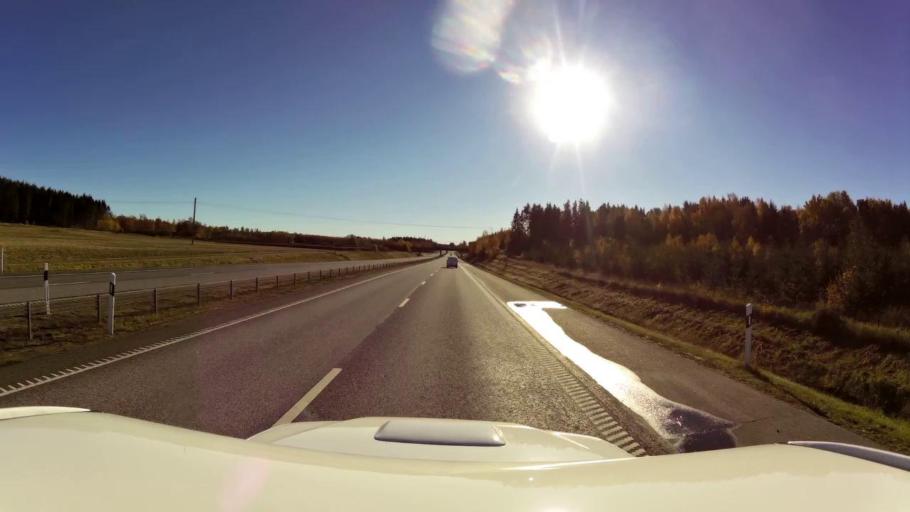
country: SE
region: OEstergoetland
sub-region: Linkopings Kommun
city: Malmslatt
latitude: 58.4176
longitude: 15.5427
